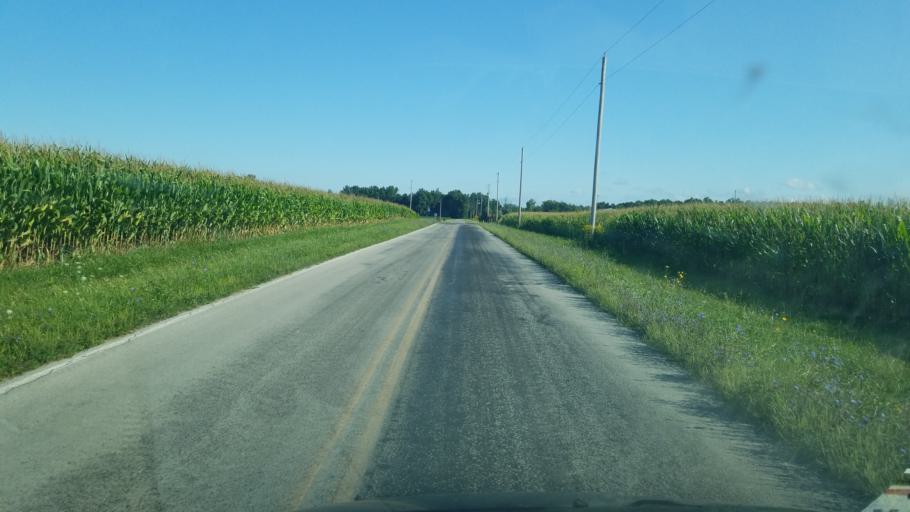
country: US
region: Ohio
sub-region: Wyandot County
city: Carey
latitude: 40.9404
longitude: -83.2997
